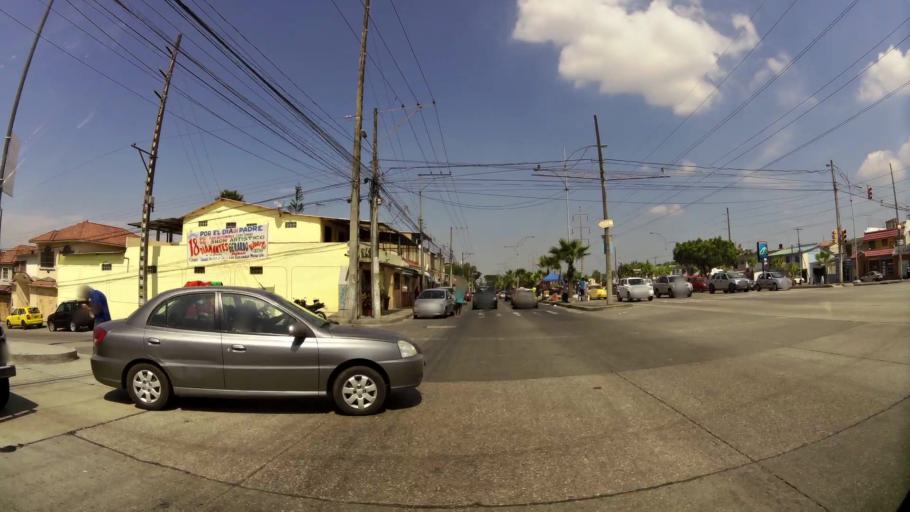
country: EC
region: Guayas
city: Eloy Alfaro
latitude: -2.1096
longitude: -79.9082
